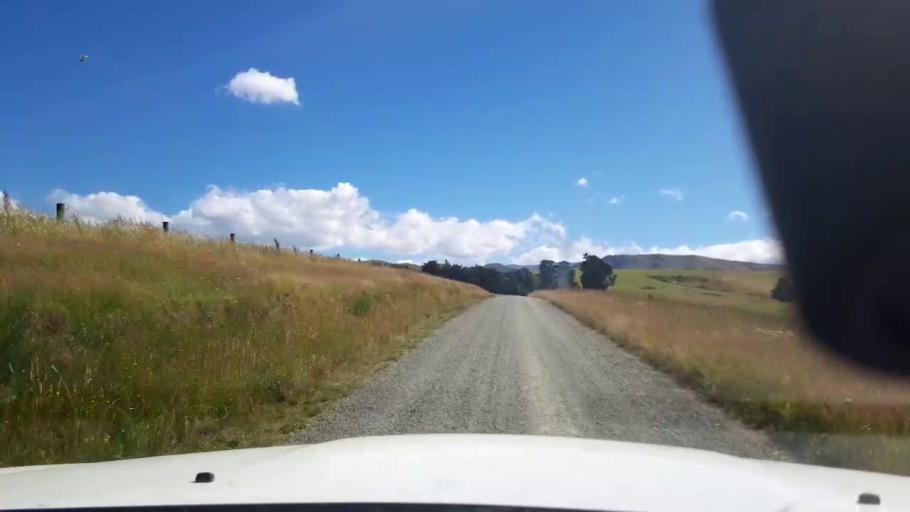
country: NZ
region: Canterbury
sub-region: Timaru District
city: Pleasant Point
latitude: -44.3138
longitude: 170.8912
